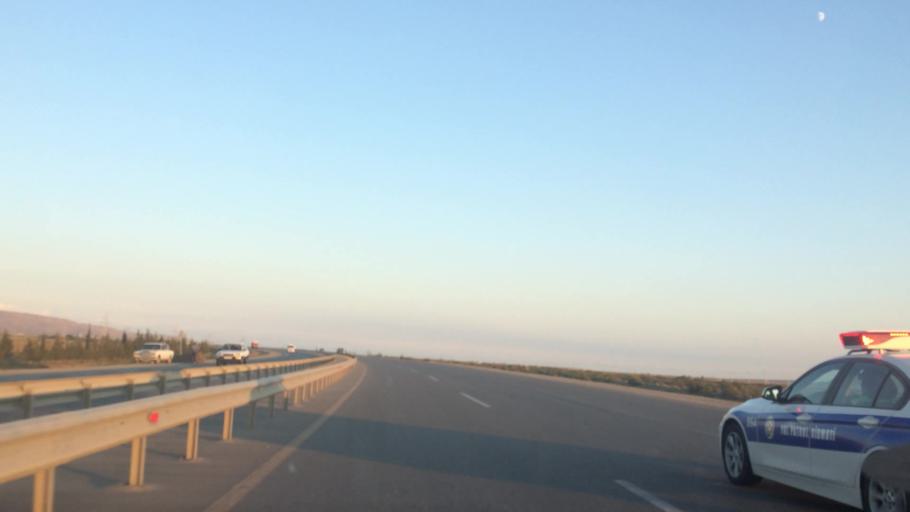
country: AZ
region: Baki
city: Qobustan
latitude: 39.9837
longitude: 49.2143
